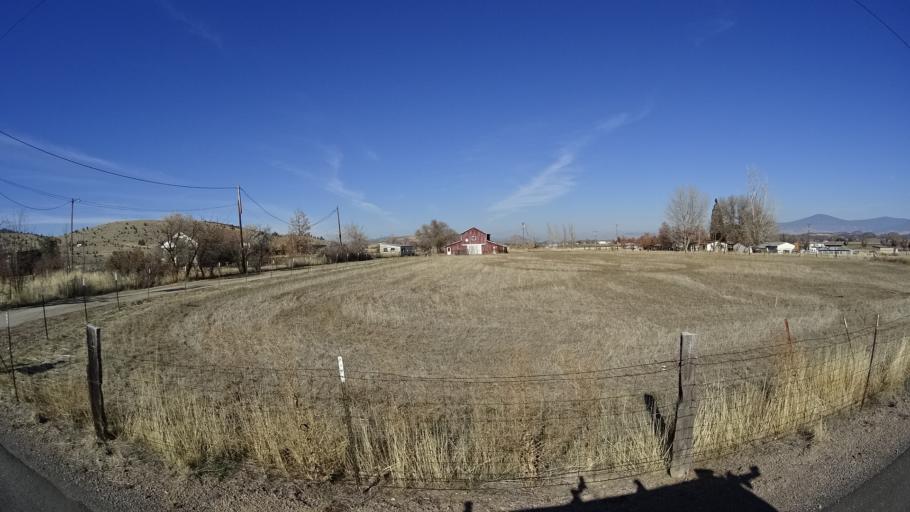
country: US
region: California
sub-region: Siskiyou County
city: Montague
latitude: 41.6330
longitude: -122.5320
